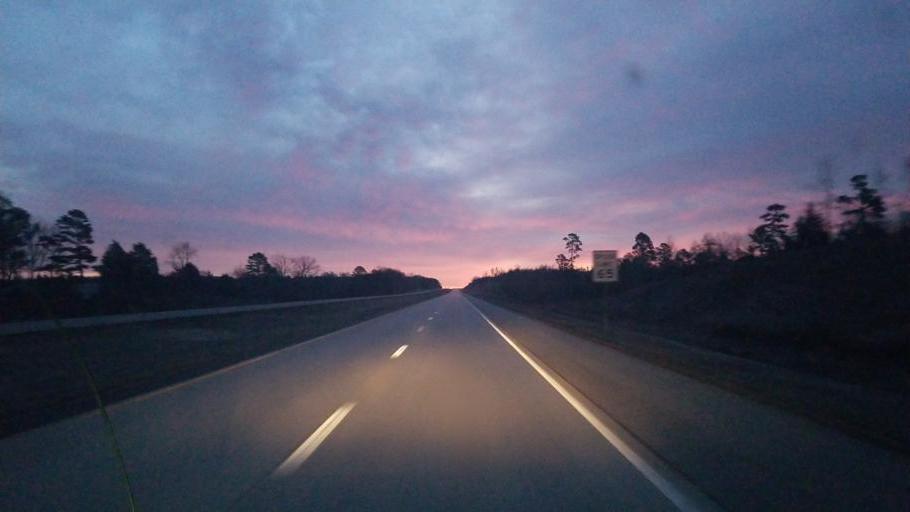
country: US
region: Missouri
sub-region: Shannon County
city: Winona
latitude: 36.9989
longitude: -91.4209
